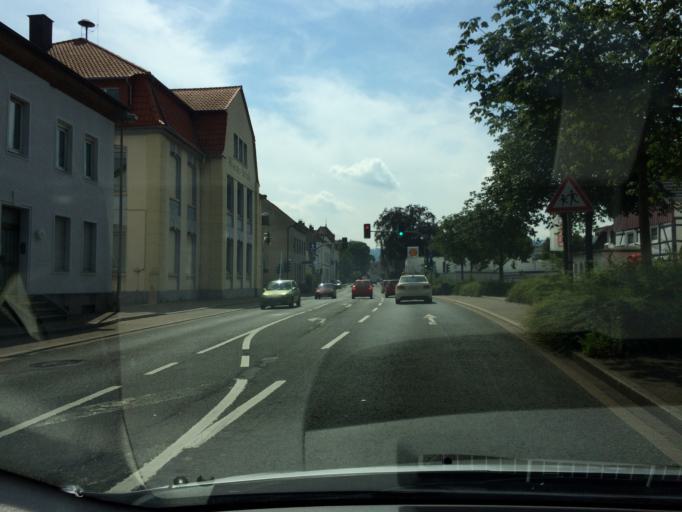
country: DE
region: North Rhine-Westphalia
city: Hemer
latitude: 51.3912
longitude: 7.7625
